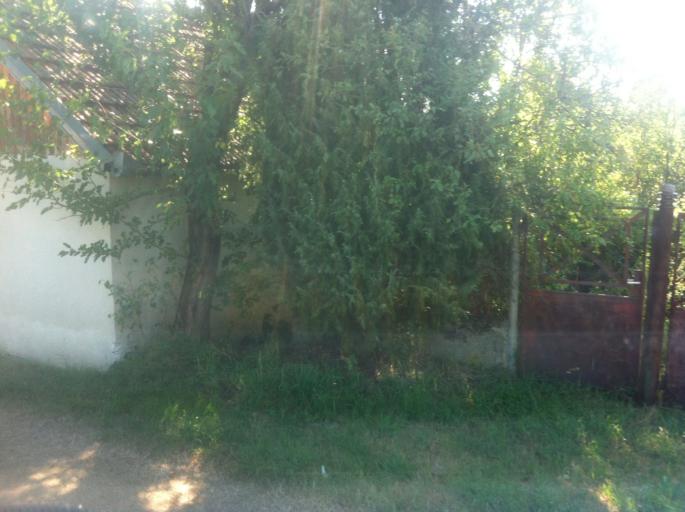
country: RO
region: Hunedoara
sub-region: Comuna Sarmizegetusa
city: Sarmizegetusa
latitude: 45.5133
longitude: 22.7724
